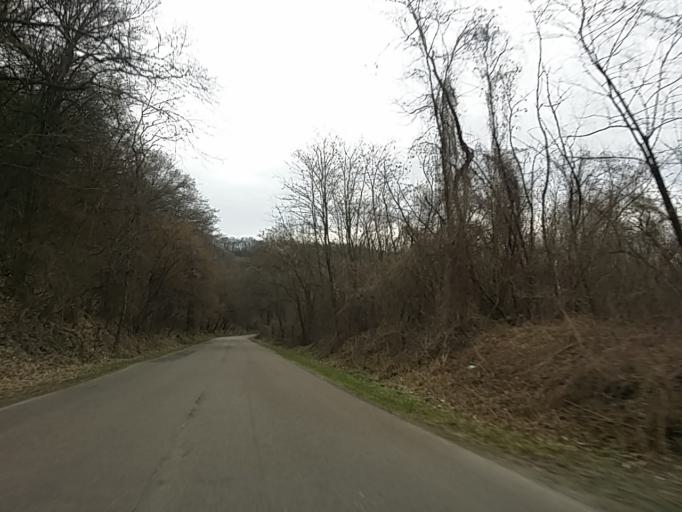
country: HU
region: Heves
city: Sirok
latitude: 47.8849
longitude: 20.1920
